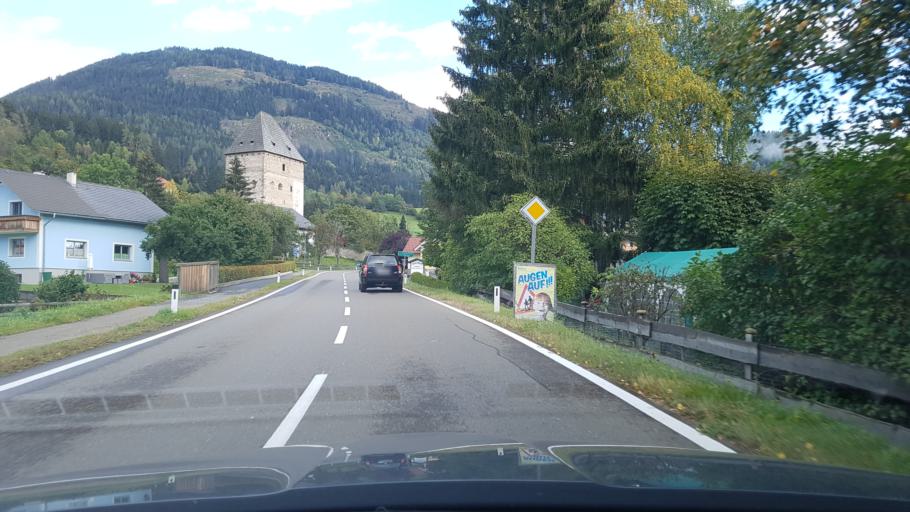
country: AT
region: Styria
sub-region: Politischer Bezirk Murau
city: Schoder
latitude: 47.1881
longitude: 14.1280
